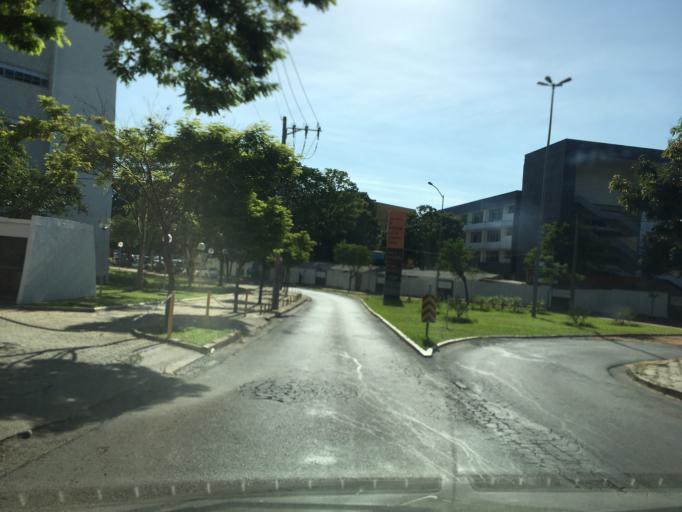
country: BR
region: Minas Gerais
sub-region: Belo Horizonte
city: Belo Horizonte
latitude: -19.8700
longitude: -43.9653
